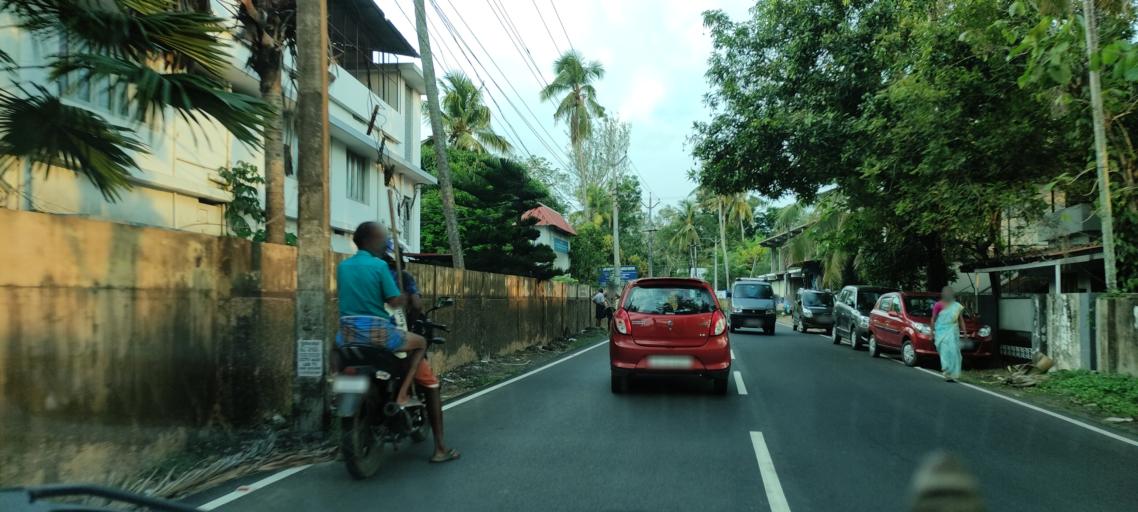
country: IN
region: Kerala
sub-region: Alappuzha
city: Kutiatodu
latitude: 9.8318
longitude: 76.3403
